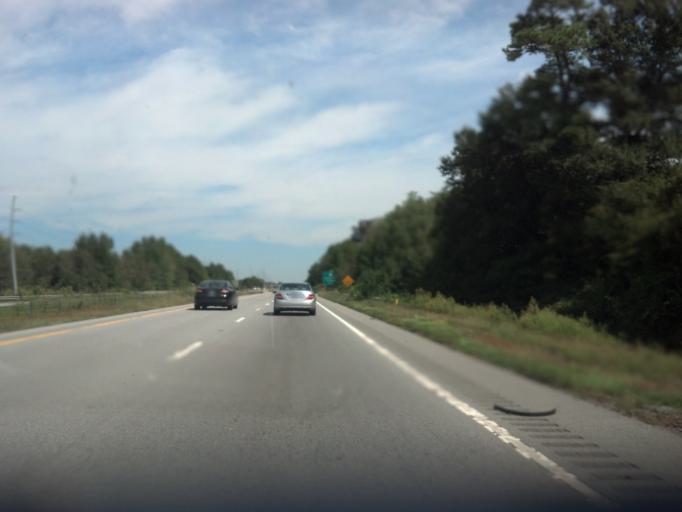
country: US
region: North Carolina
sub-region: Pitt County
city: Greenville
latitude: 35.6413
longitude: -77.4249
